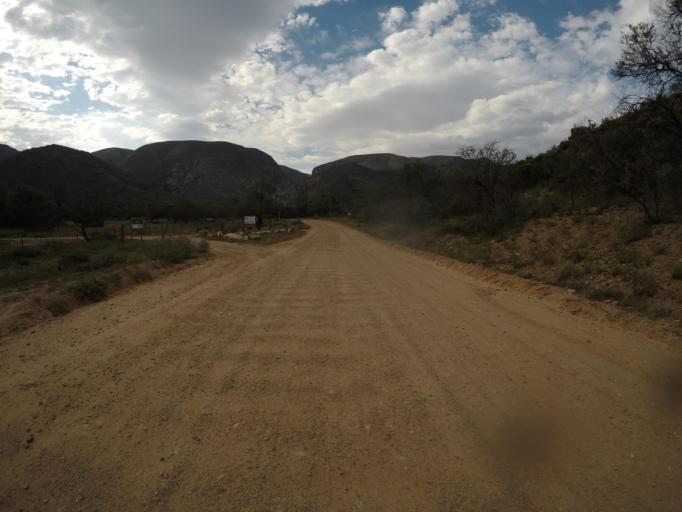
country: ZA
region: Eastern Cape
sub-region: Cacadu District Municipality
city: Kareedouw
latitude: -33.5847
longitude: 24.1655
